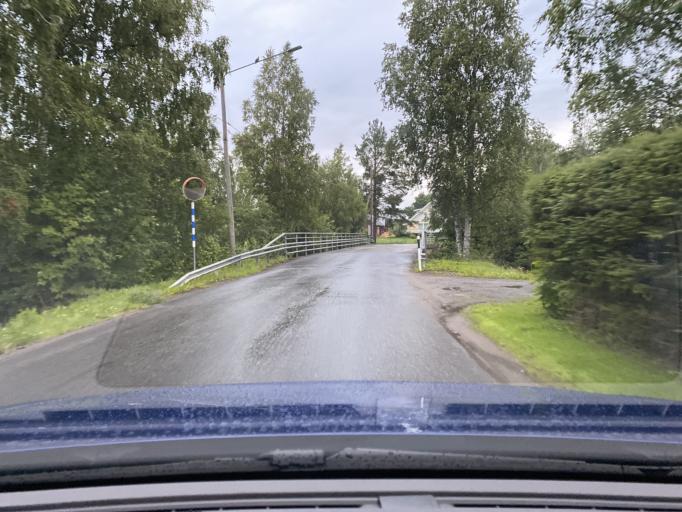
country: FI
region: Ostrobothnia
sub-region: Kyroenmaa
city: Laihia
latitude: 62.9823
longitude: 21.9922
